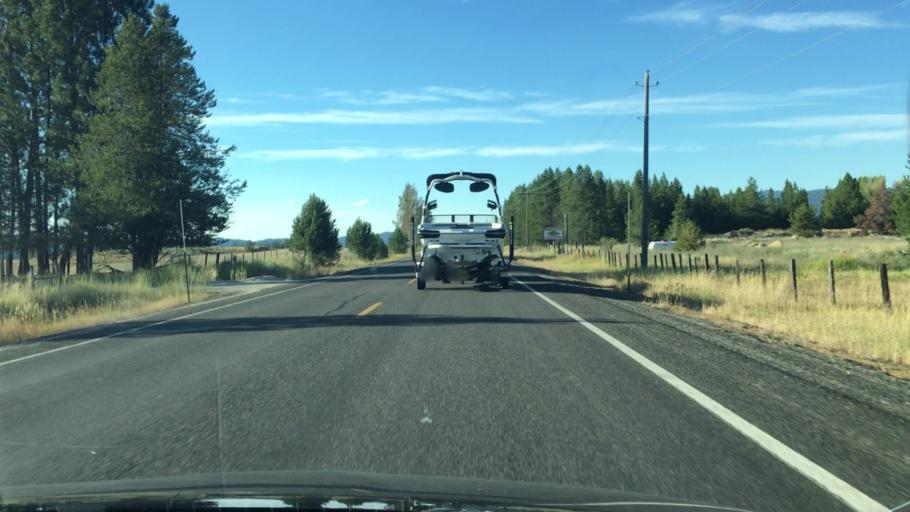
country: US
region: Idaho
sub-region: Valley County
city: Cascade
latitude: 44.4697
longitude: -115.9991
